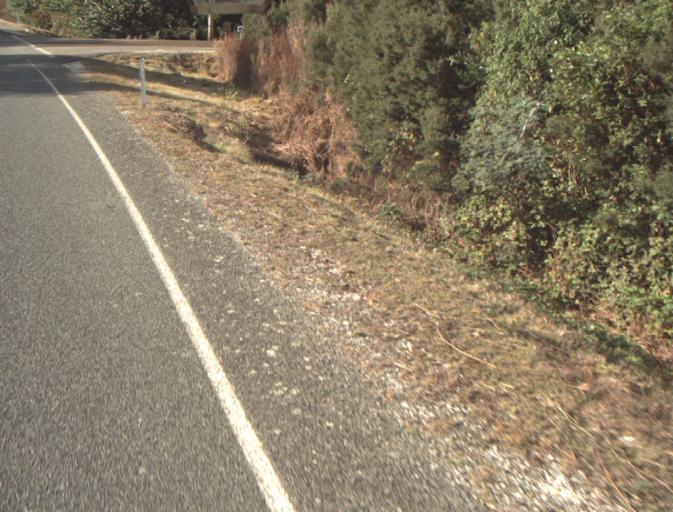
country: AU
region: Tasmania
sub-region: Launceston
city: Mayfield
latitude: -41.2794
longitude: 147.2202
